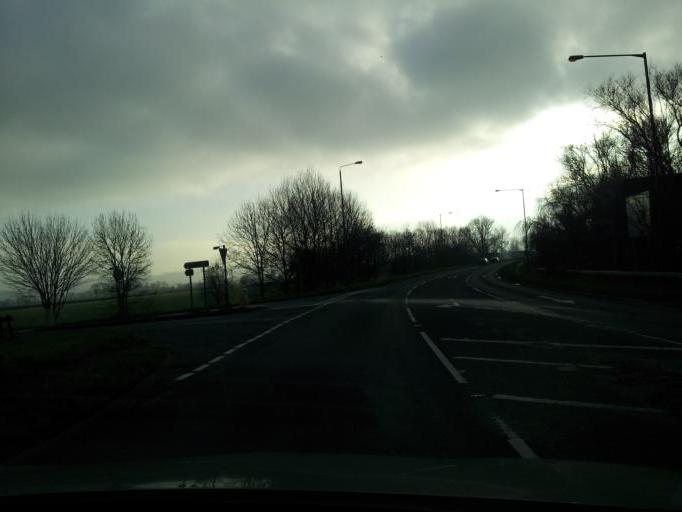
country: GB
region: England
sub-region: Derbyshire
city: Rodsley
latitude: 52.8819
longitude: -1.7533
